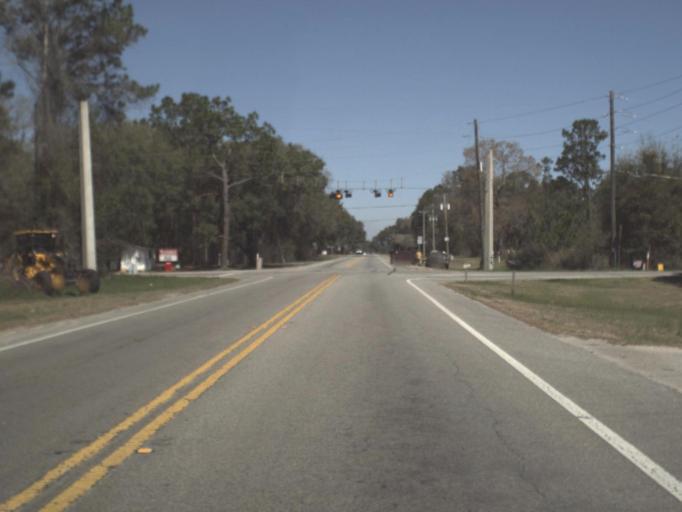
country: US
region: Florida
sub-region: Leon County
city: Woodville
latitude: 30.3241
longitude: -84.3115
